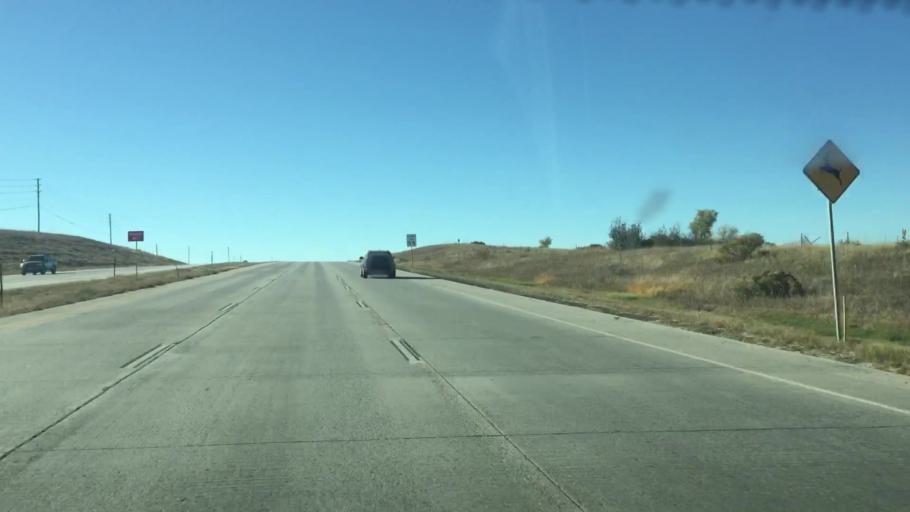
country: US
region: Colorado
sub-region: Douglas County
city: The Pinery
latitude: 39.4736
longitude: -104.7585
